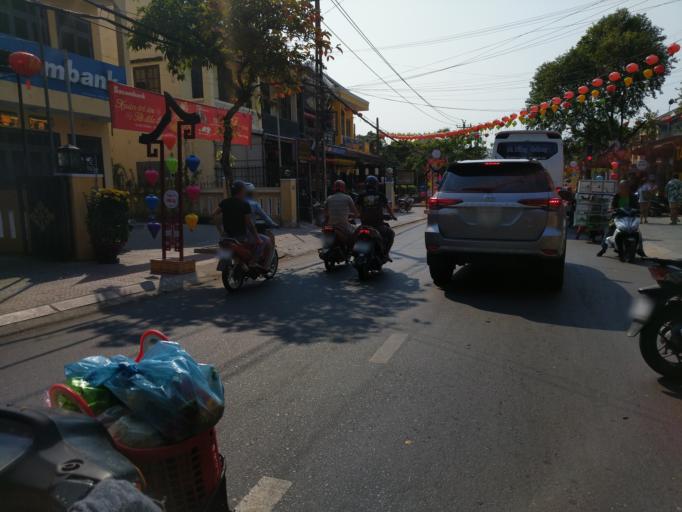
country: VN
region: Quang Nam
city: Hoi An
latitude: 15.8799
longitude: 108.3273
